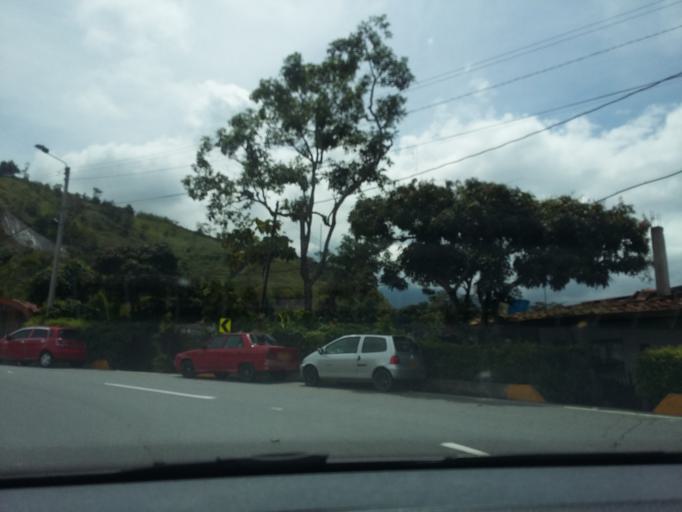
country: CO
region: Santander
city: Bucaramanga
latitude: 7.1109
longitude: -73.0829
